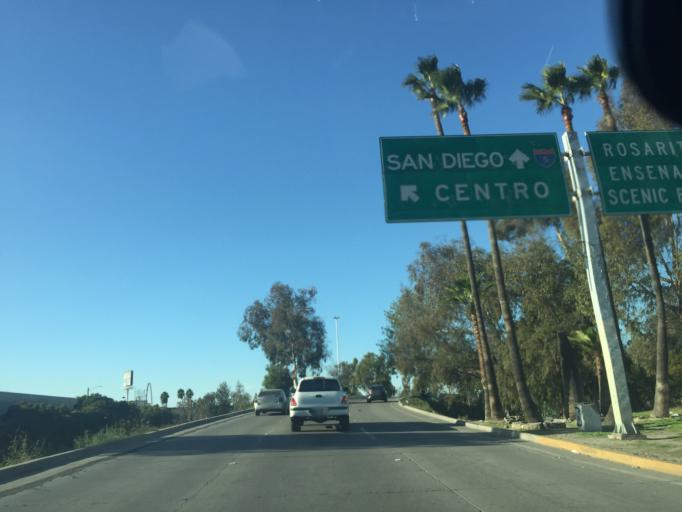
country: MX
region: Baja California
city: Tijuana
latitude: 32.5323
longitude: -117.0279
